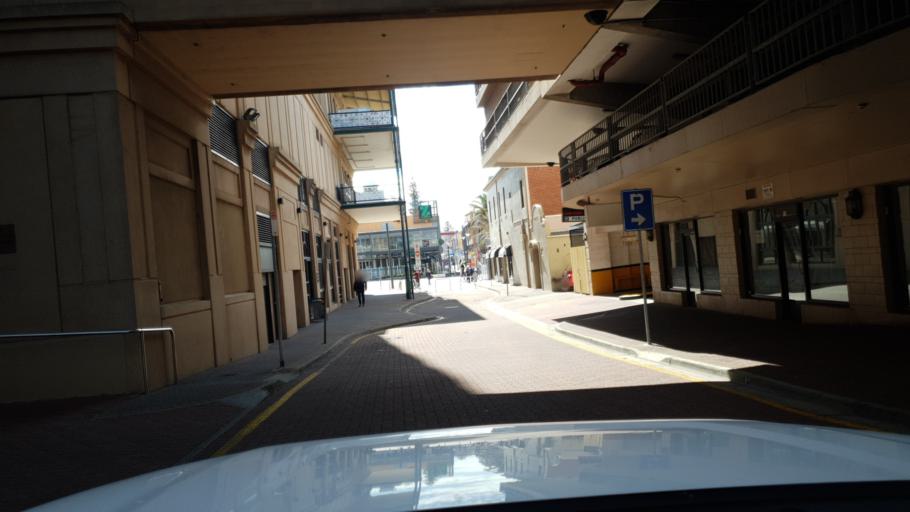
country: AU
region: South Australia
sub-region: Adelaide
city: Glenelg
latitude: -34.9811
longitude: 138.5116
